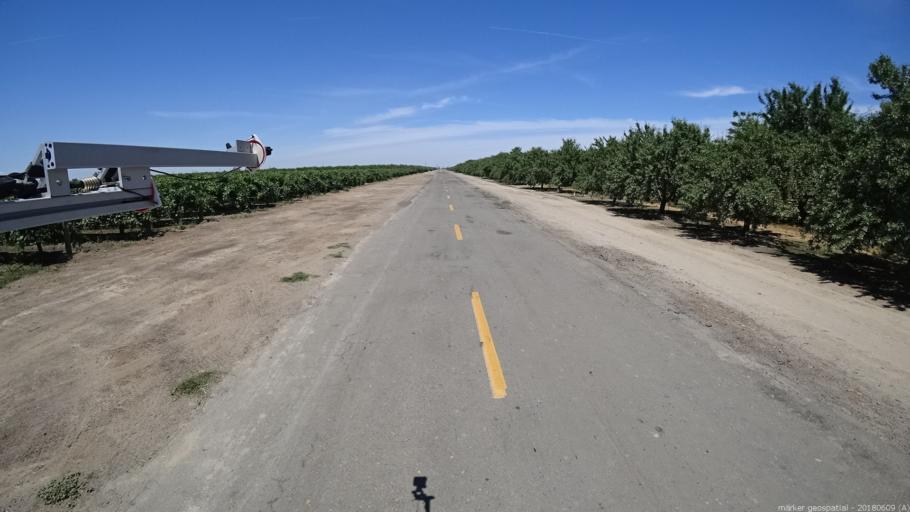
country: US
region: California
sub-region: Madera County
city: Madera
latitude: 36.9382
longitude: -120.1945
